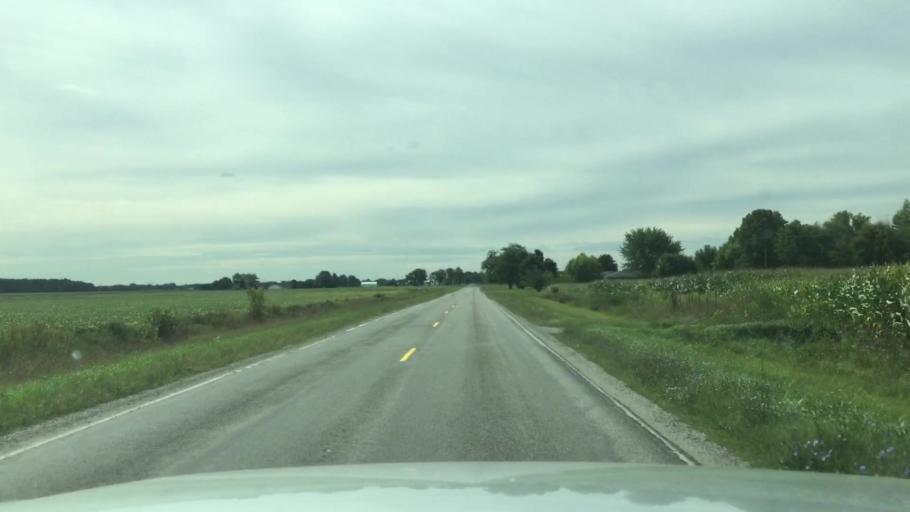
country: US
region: Michigan
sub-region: Genesee County
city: Montrose
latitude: 43.1411
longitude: -83.9883
